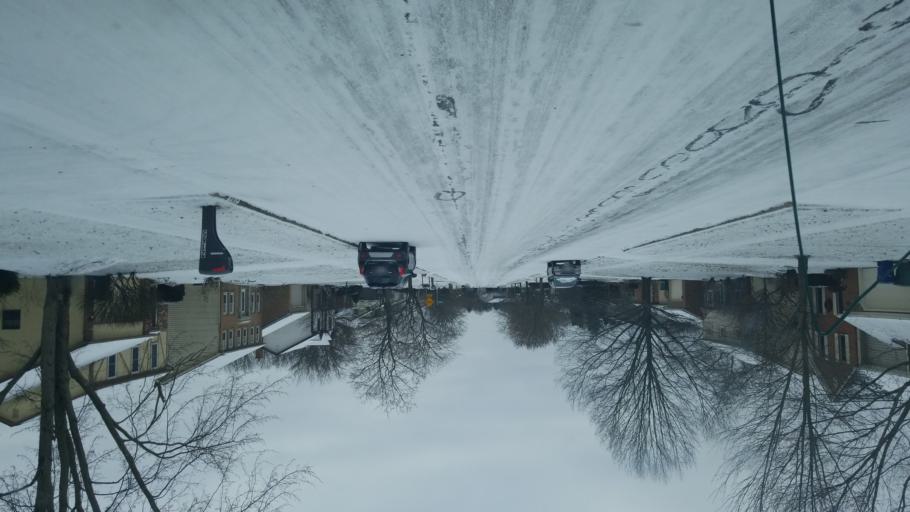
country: US
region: Ohio
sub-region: Delaware County
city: Powell
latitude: 40.1275
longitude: -83.0738
